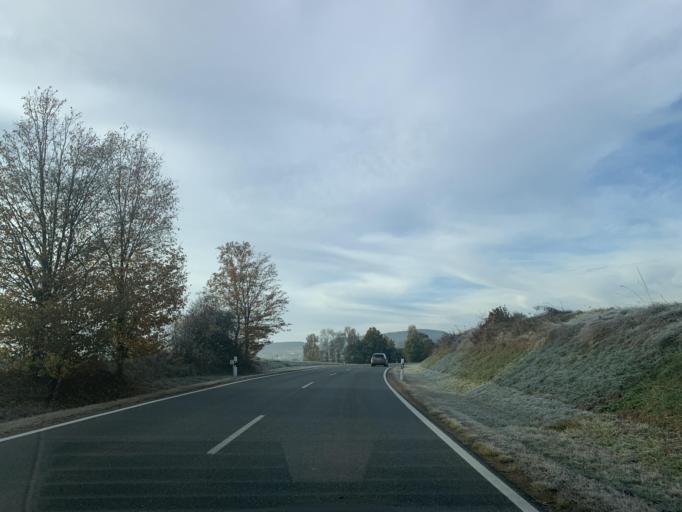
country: DE
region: Bavaria
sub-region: Upper Palatinate
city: Neunburg vorm Wald
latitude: 49.3639
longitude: 12.3784
